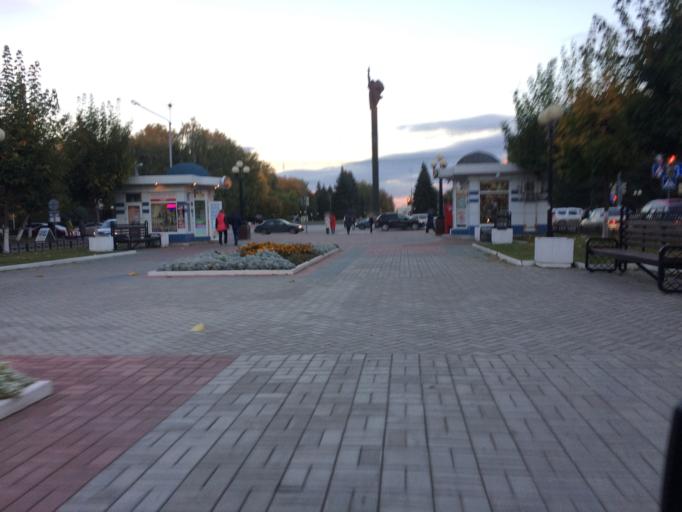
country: RU
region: Mariy-El
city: Yoshkar-Ola
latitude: 56.6374
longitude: 47.8855
